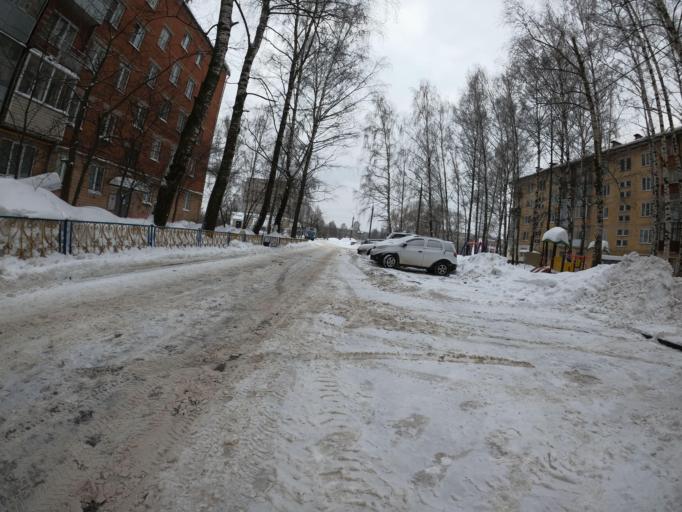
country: RU
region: Moskovskaya
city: Elektrogorsk
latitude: 55.8753
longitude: 38.7862
